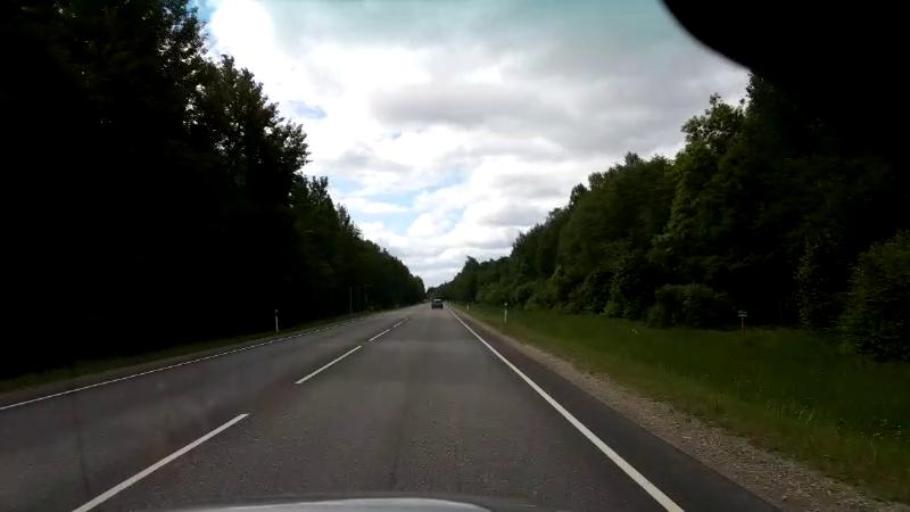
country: EE
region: Paernumaa
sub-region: Halinga vald
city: Parnu-Jaagupi
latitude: 58.6085
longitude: 24.5123
